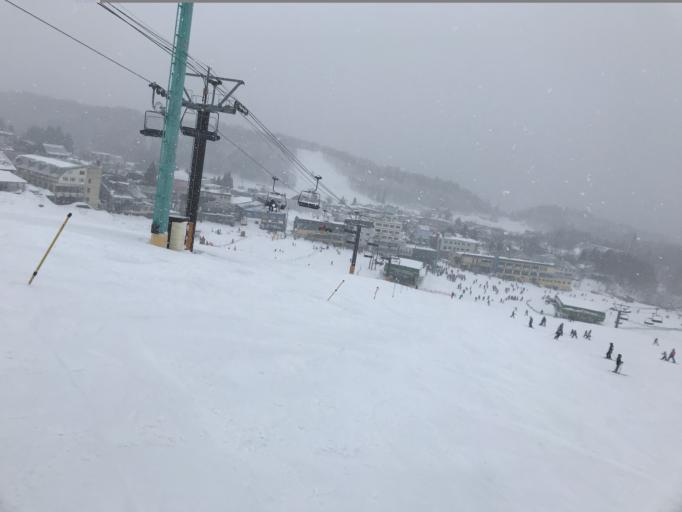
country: JP
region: Nagano
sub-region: Kitaazumi Gun
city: Hakuba
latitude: 36.7484
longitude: 137.8667
